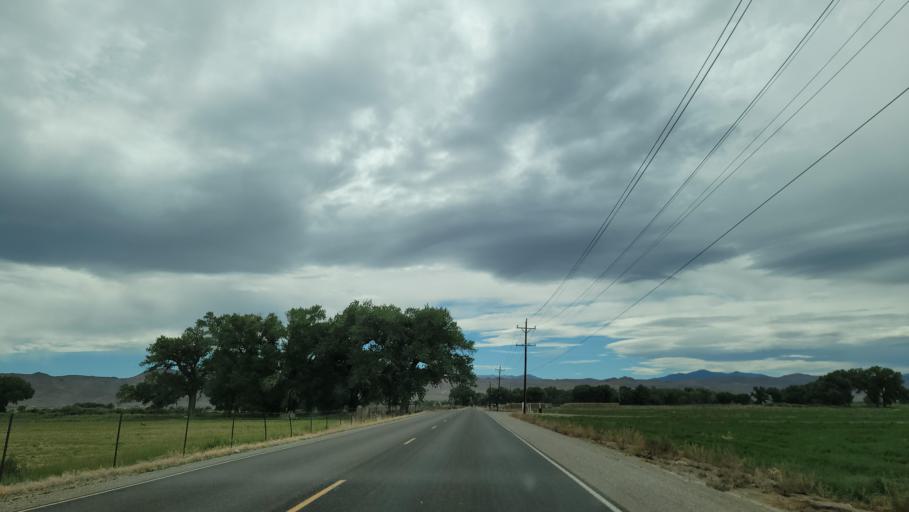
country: US
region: Nevada
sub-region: Lyon County
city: Yerington
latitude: 39.0481
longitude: -119.1683
